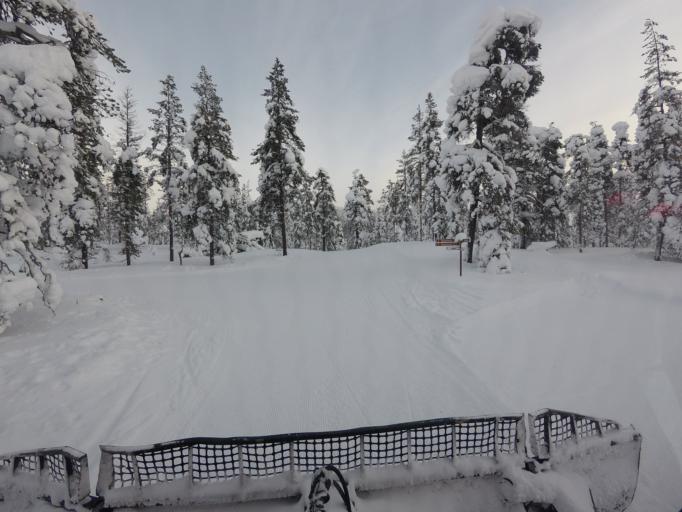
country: FI
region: Lapland
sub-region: Tunturi-Lappi
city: Kolari
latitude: 67.6557
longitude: 24.2499
